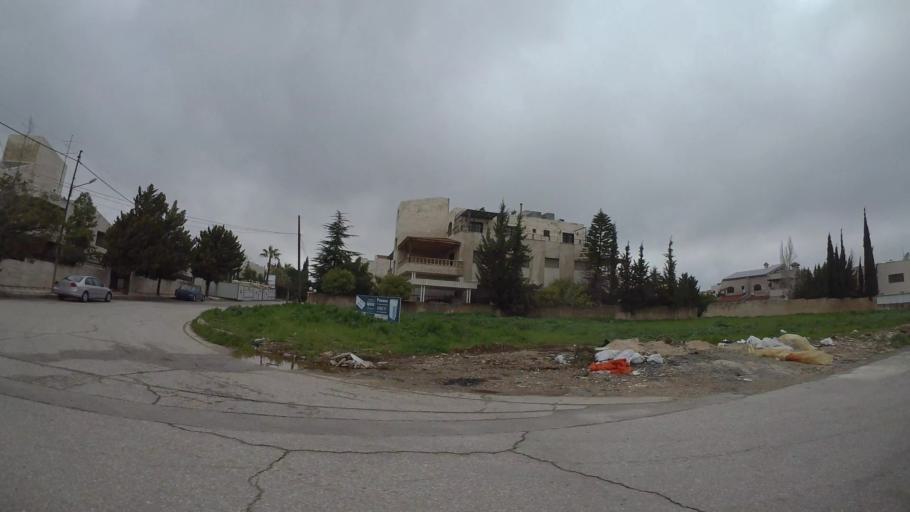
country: JO
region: Amman
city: Amman
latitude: 31.9463
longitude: 35.8987
